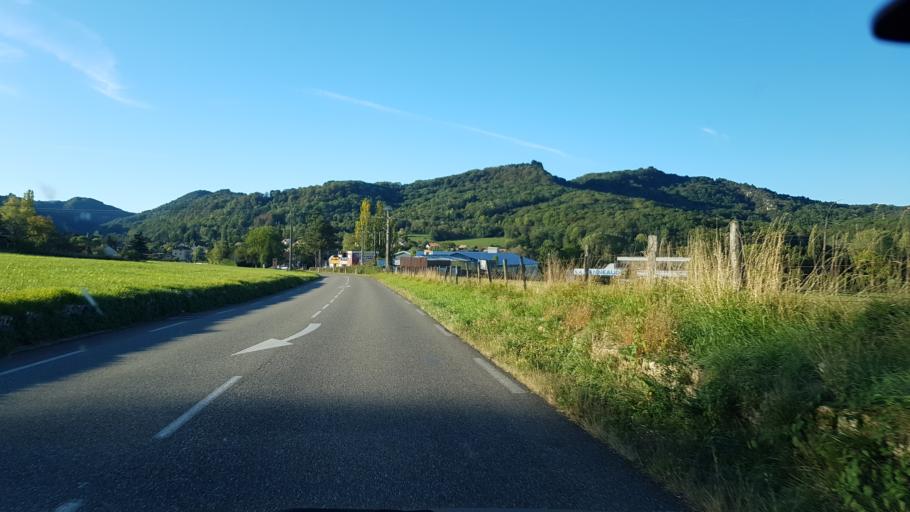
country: FR
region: Franche-Comte
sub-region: Departement du Jura
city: Lons-le-Saunier
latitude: 46.6539
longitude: 5.5380
